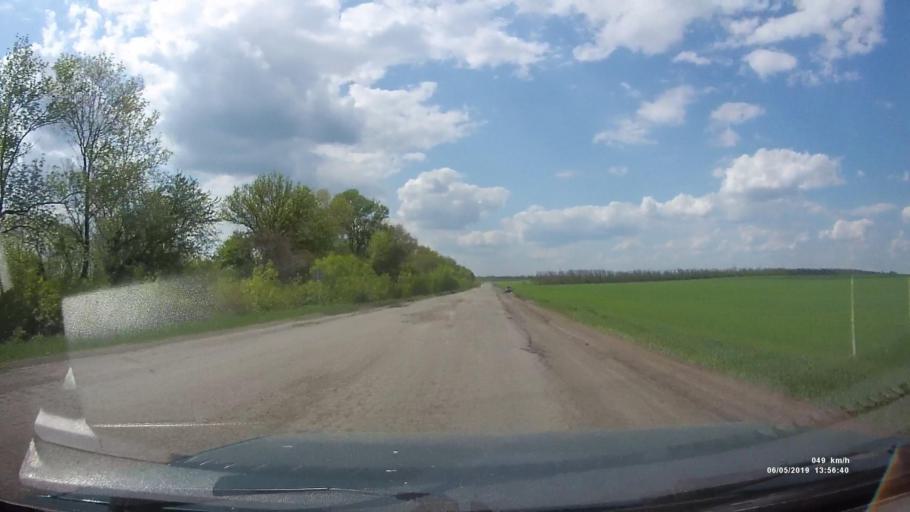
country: RU
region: Rostov
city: Melikhovskaya
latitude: 47.6820
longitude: 40.4290
